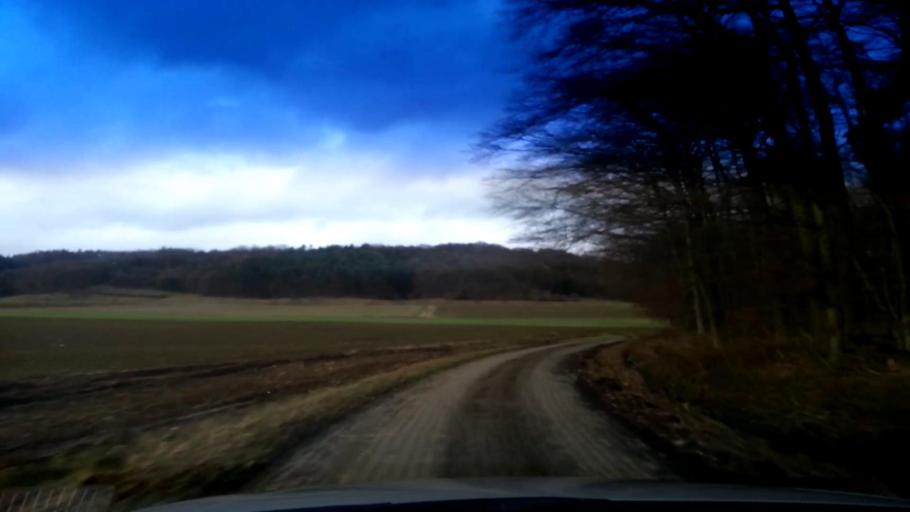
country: DE
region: Bavaria
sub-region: Upper Franconia
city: Schesslitz
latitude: 50.0087
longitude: 11.0280
